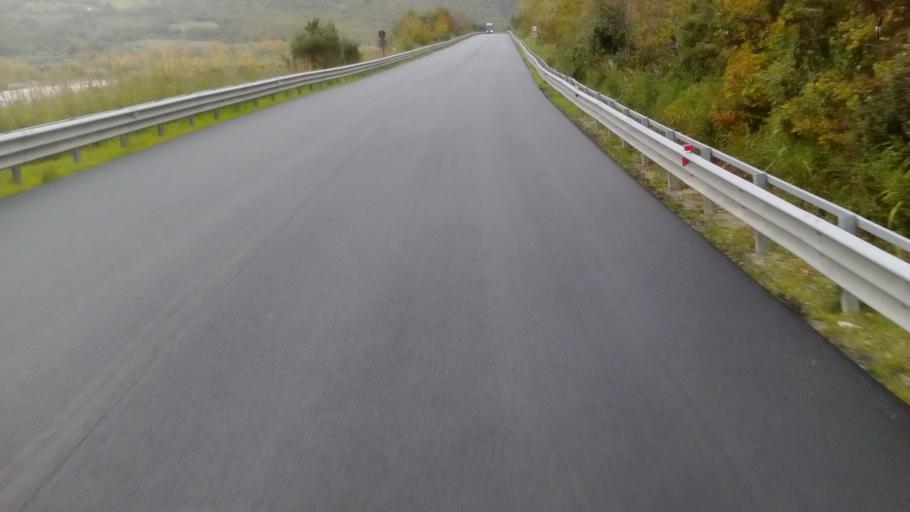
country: IT
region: Abruzzo
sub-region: Provincia di Chieti
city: Dogliola
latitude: 41.9236
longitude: 14.6635
